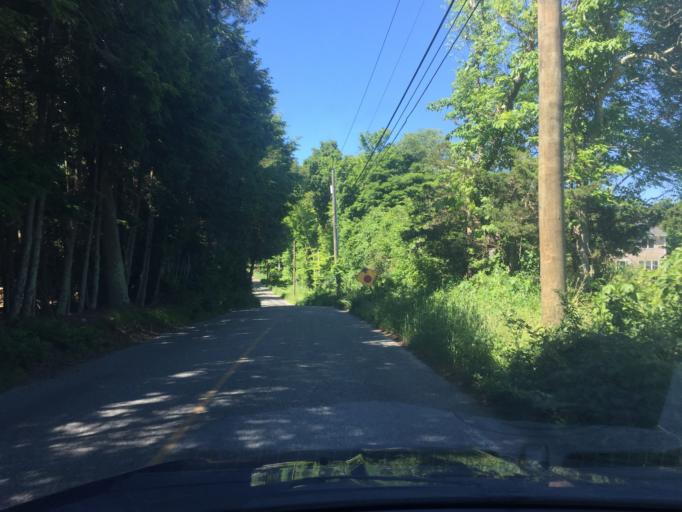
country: US
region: Rhode Island
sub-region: Washington County
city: Hopkinton
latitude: 41.4667
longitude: -71.8144
